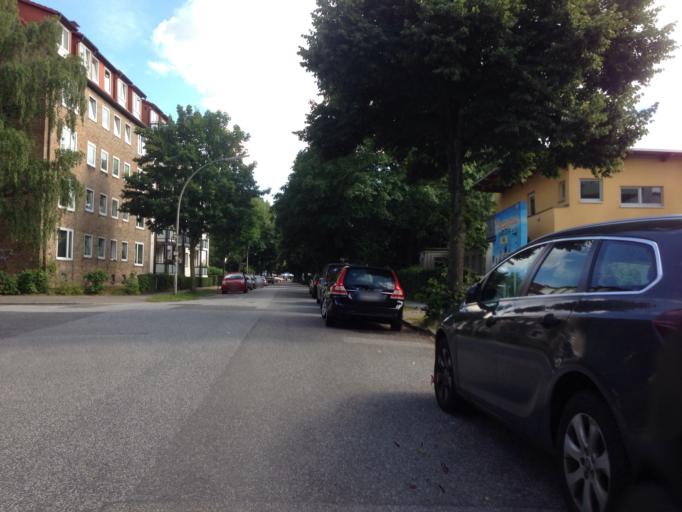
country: DE
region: Hamburg
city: Hamburg
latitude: 53.5782
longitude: 10.0346
